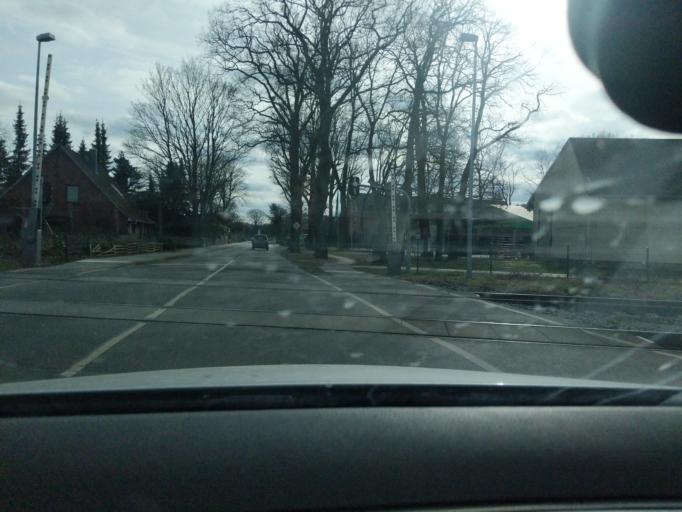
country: DE
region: Lower Saxony
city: Himmelpforten
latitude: 53.6223
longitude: 9.3166
